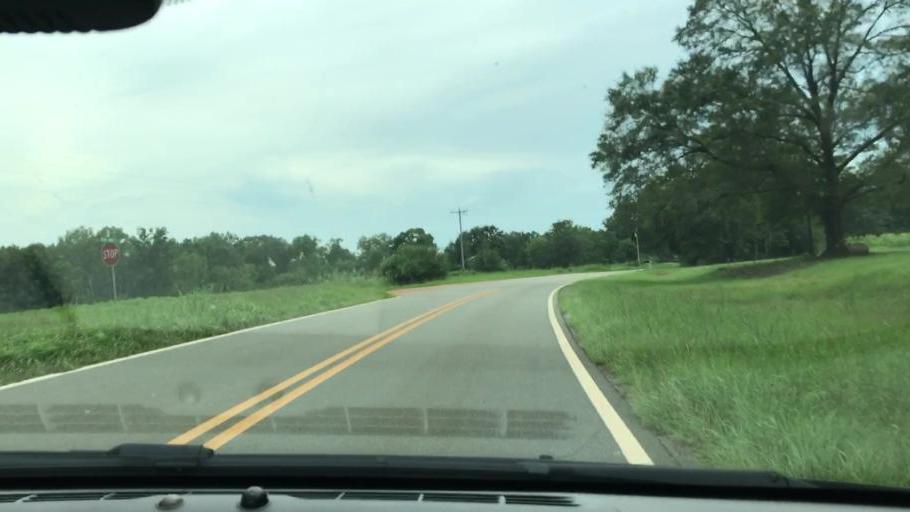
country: US
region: Georgia
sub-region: Early County
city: Blakely
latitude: 31.4437
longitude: -84.9134
